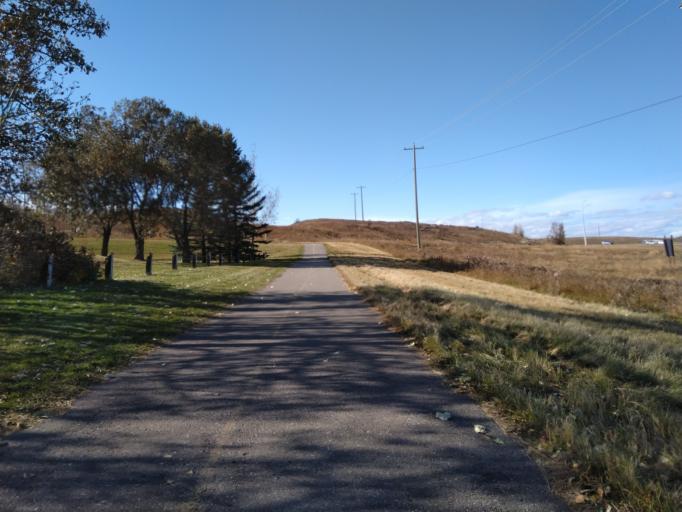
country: CA
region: Alberta
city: Calgary
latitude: 51.1541
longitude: -114.1156
